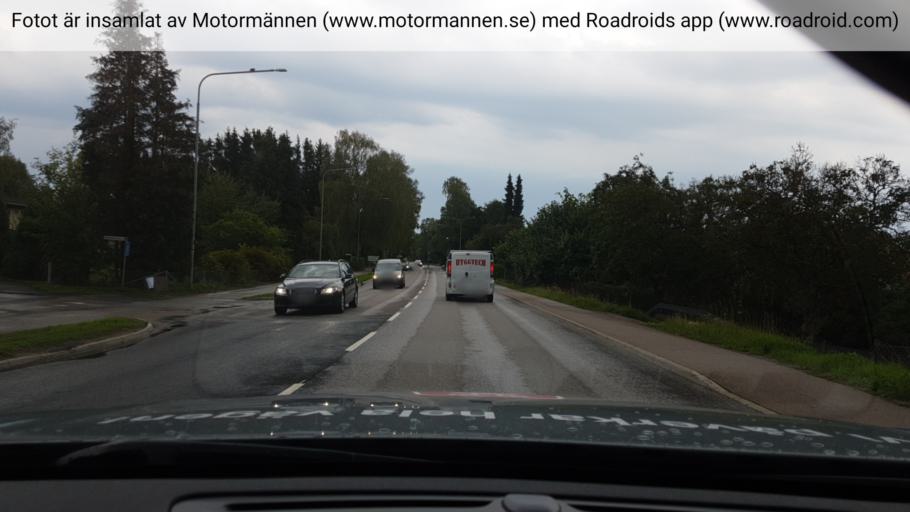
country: SE
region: Uppsala
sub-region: Habo Kommun
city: Balsta
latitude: 59.5737
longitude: 17.5191
